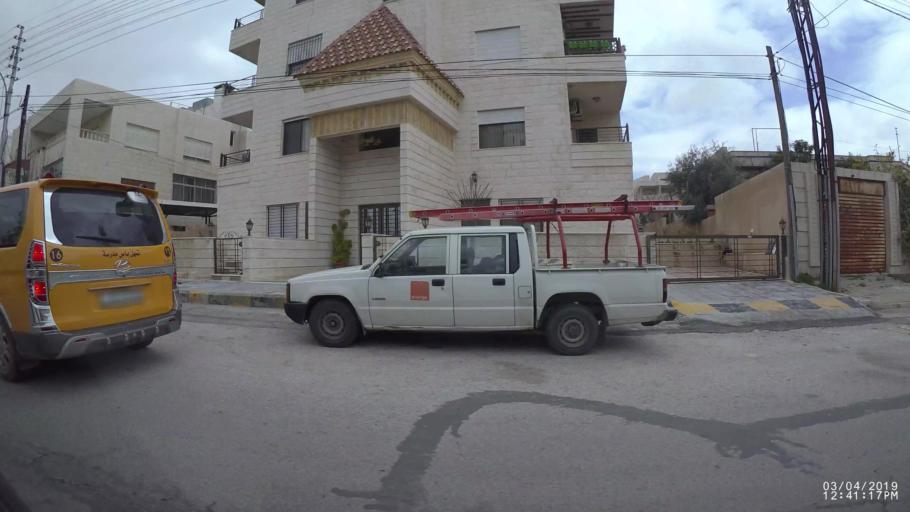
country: JO
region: Amman
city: Wadi as Sir
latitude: 31.9616
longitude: 35.8350
